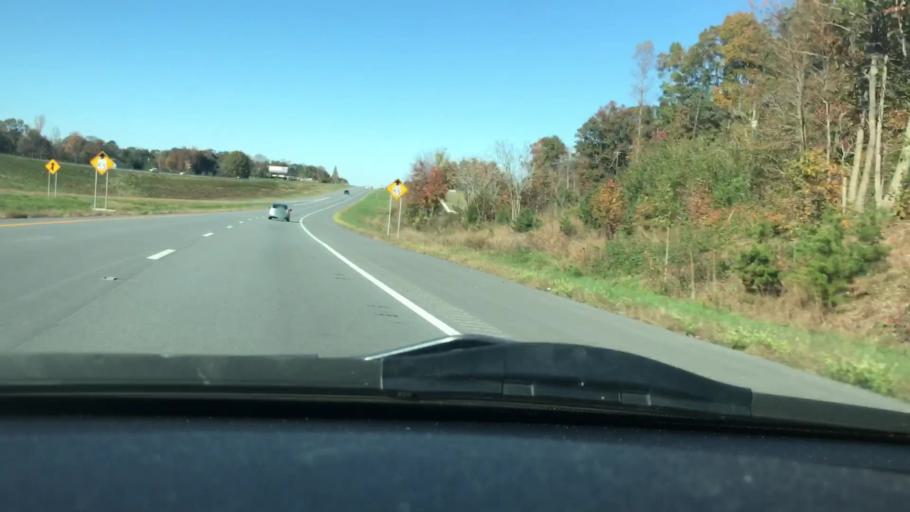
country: US
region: North Carolina
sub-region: Guilford County
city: Stokesdale
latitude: 36.2844
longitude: -79.9392
